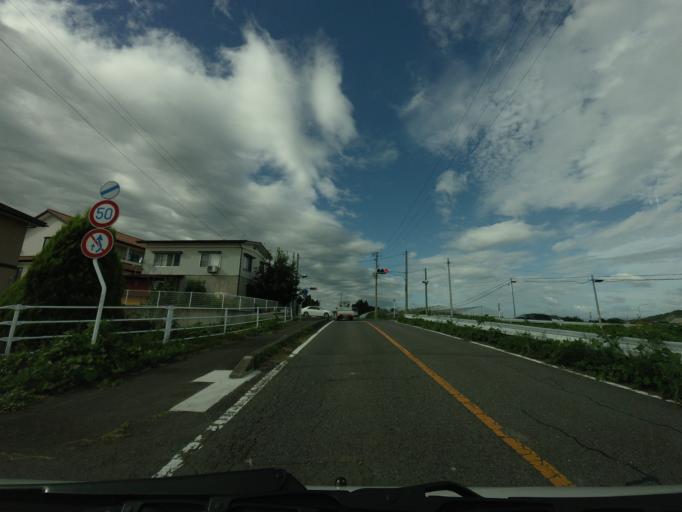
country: JP
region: Fukushima
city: Motomiya
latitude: 37.5424
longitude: 140.3780
